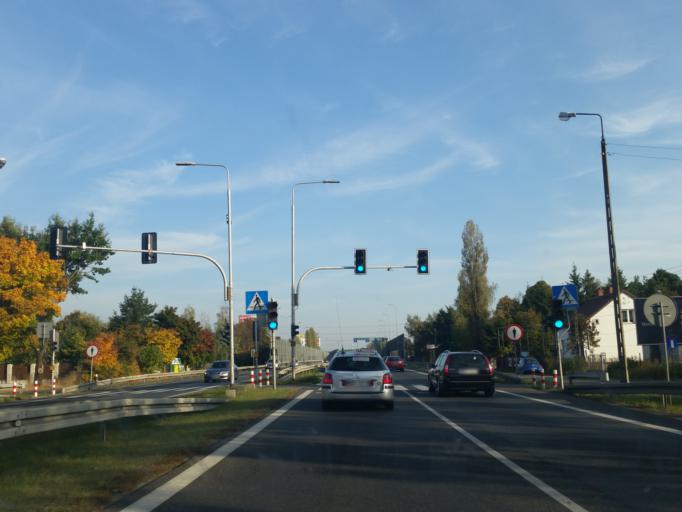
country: PL
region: Masovian Voivodeship
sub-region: Powiat warszawski zachodni
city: Lomianki
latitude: 52.3311
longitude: 20.8935
